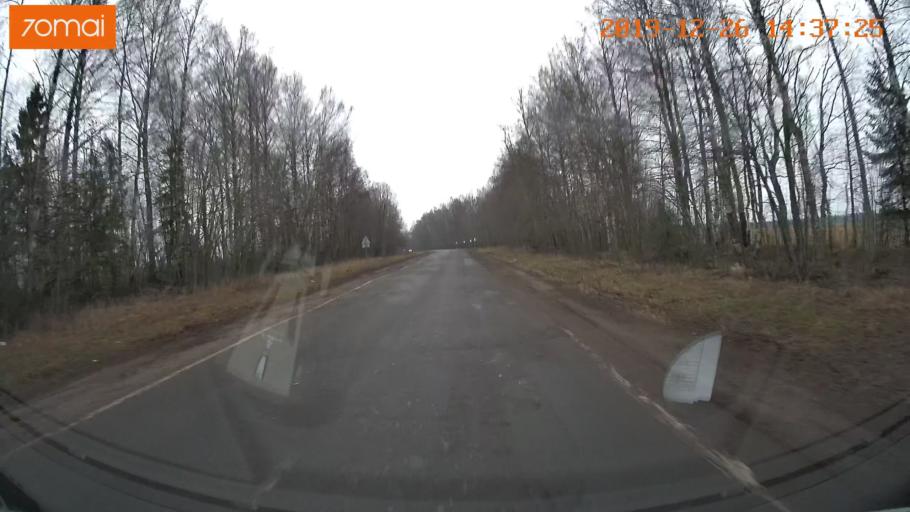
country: RU
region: Jaroslavl
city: Poshekhon'ye
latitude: 58.4025
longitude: 38.9724
